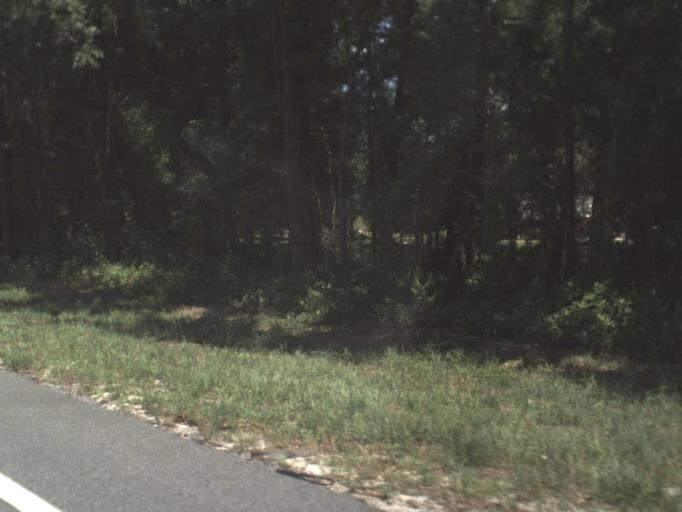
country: US
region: Florida
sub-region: Dixie County
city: Cross City
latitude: 29.8588
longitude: -82.9615
